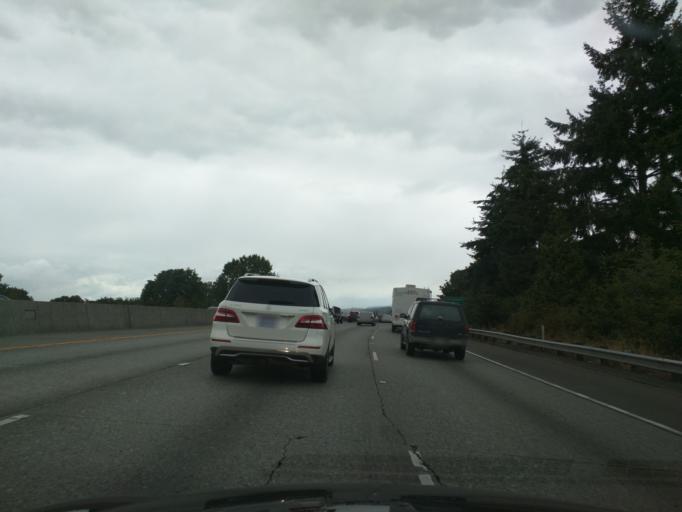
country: US
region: Washington
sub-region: Snohomish County
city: Everett
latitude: 47.9911
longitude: -122.1821
